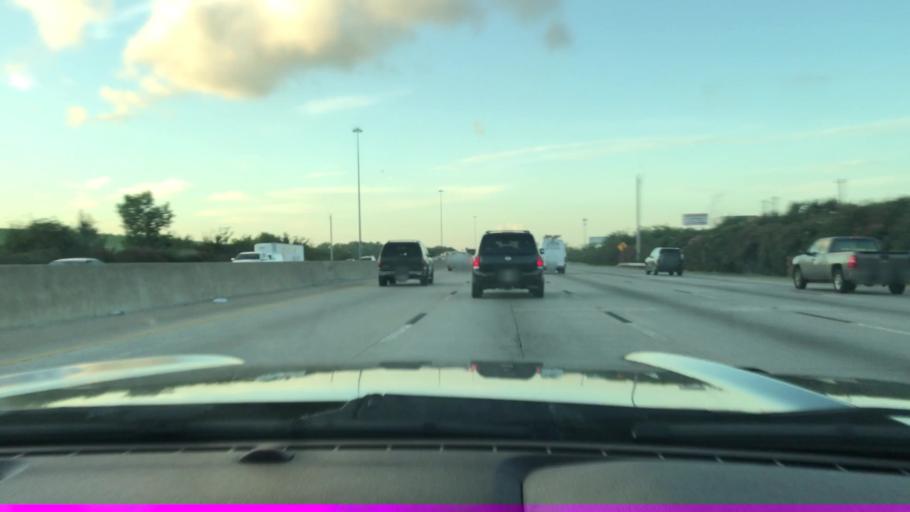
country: US
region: Texas
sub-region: Harris County
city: Jacinto City
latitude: 29.7510
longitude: -95.2651
